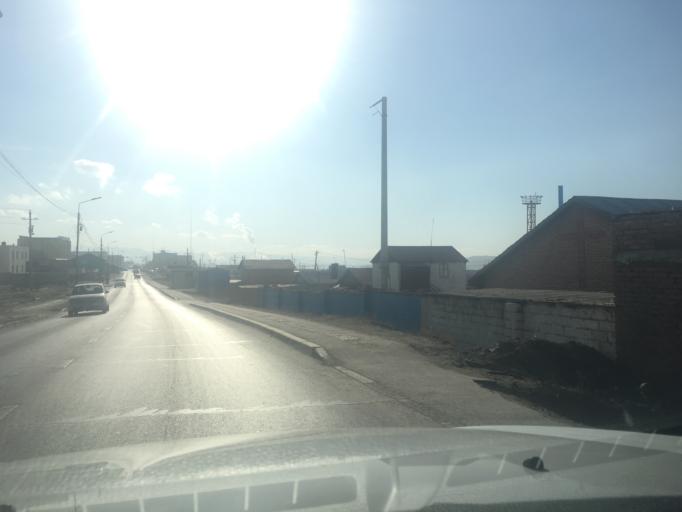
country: MN
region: Ulaanbaatar
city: Ulaanbaatar
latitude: 47.9595
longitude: 106.8266
